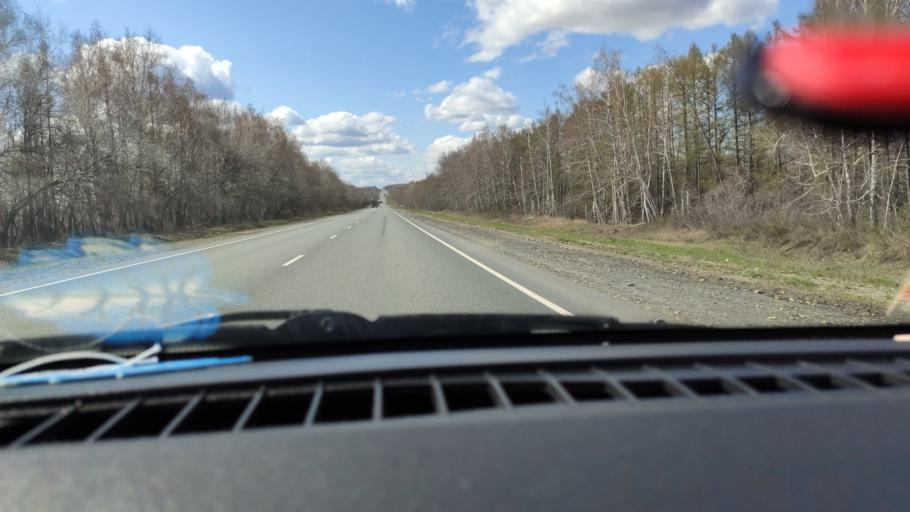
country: RU
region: Saratov
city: Khvalynsk
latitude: 52.5747
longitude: 48.1078
